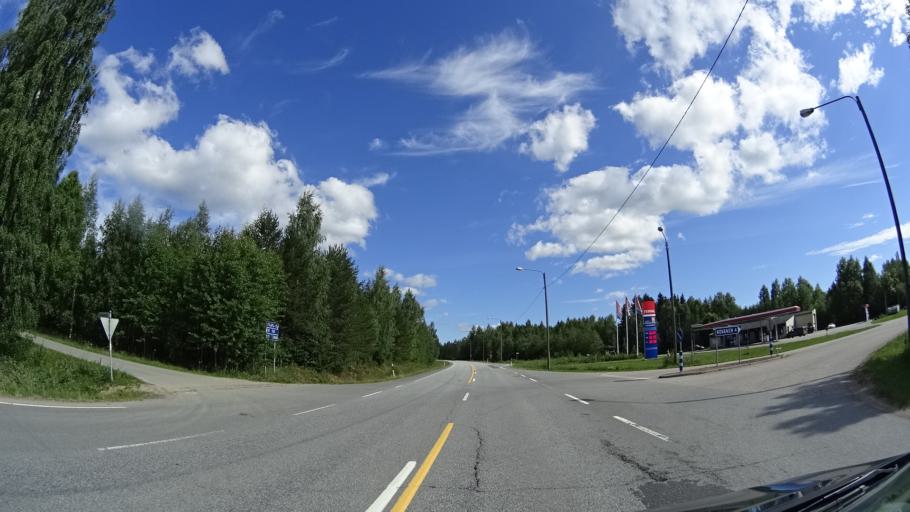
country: FI
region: Pirkanmaa
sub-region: Luoteis-Pirkanmaa
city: Kihnioe
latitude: 62.1755
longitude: 23.1695
